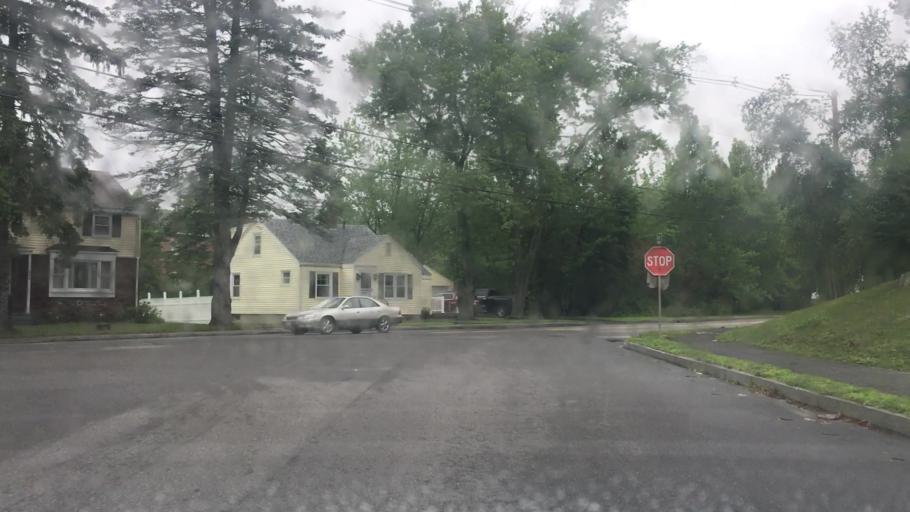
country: US
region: Maine
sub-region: Cumberland County
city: Portland
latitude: 43.6871
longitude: -70.2668
